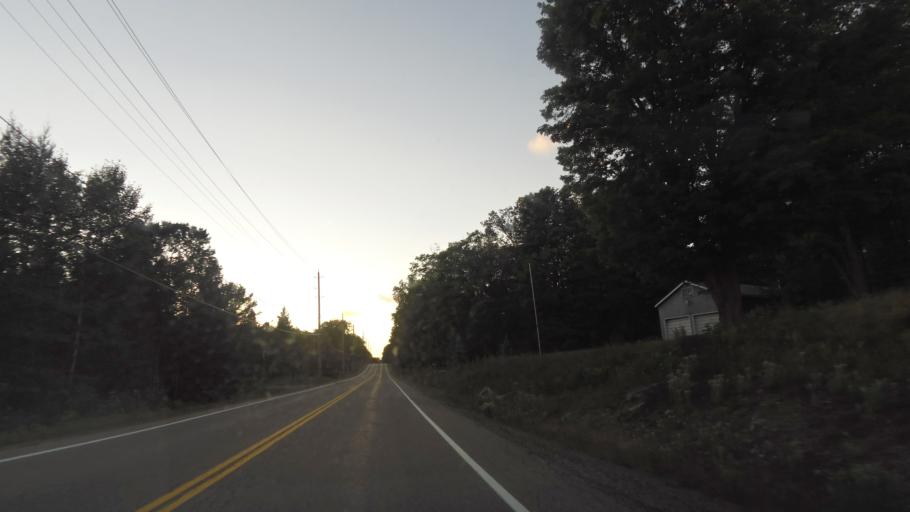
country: CA
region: Ontario
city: Bancroft
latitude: 45.0284
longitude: -78.4016
